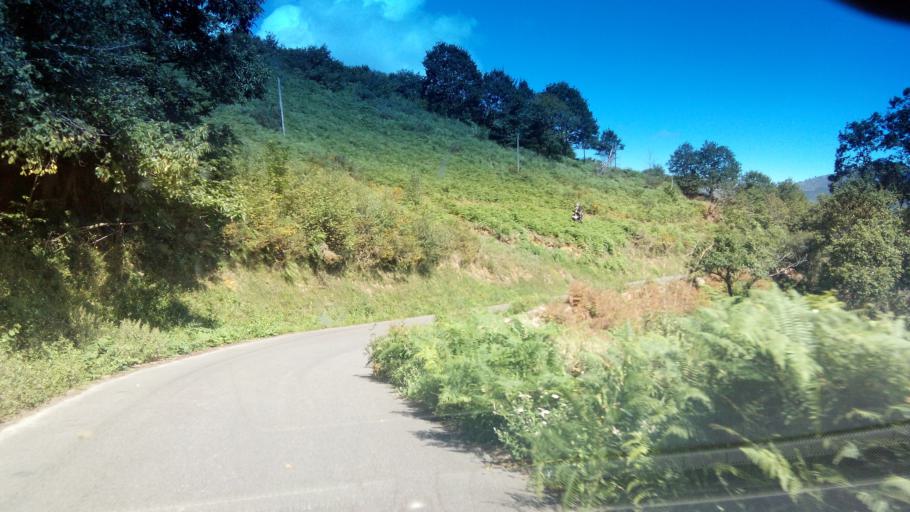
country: ES
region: Asturias
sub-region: Province of Asturias
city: Parres
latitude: 43.3727
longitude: -5.1730
